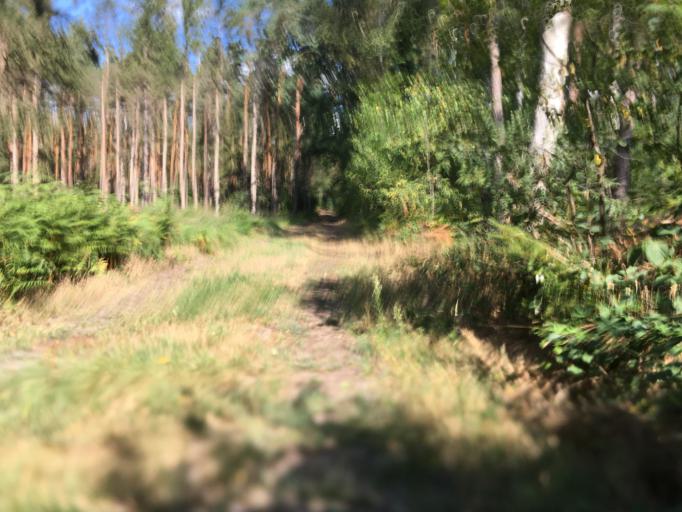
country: DE
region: Brandenburg
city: Zehdenick
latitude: 53.0015
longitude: 13.3738
